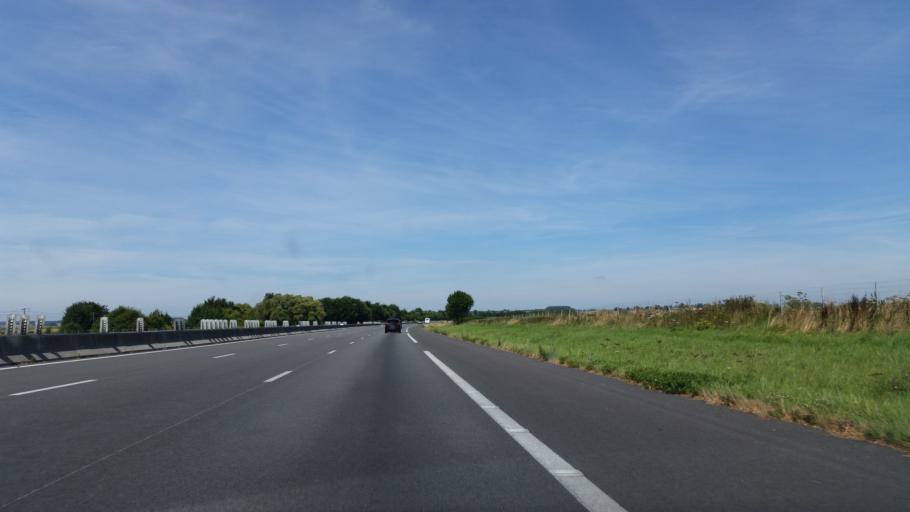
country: FR
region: Nord-Pas-de-Calais
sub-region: Departement du Pas-de-Calais
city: Bapaume
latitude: 50.0427
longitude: 2.8786
